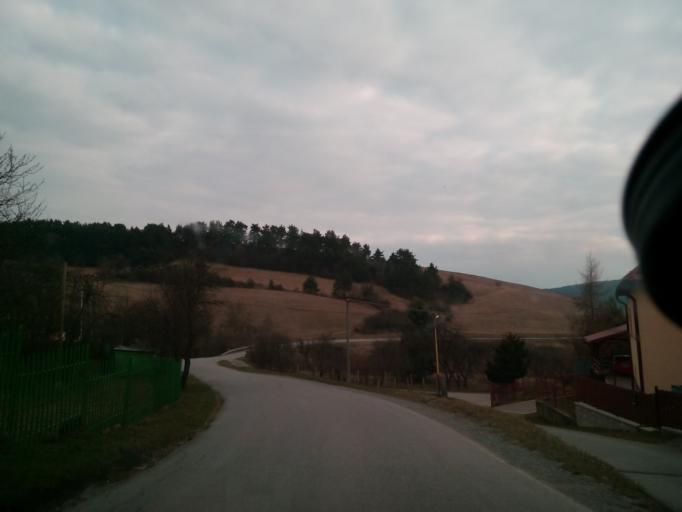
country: SK
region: Presovsky
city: Sabinov
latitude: 49.0442
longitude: 21.0203
